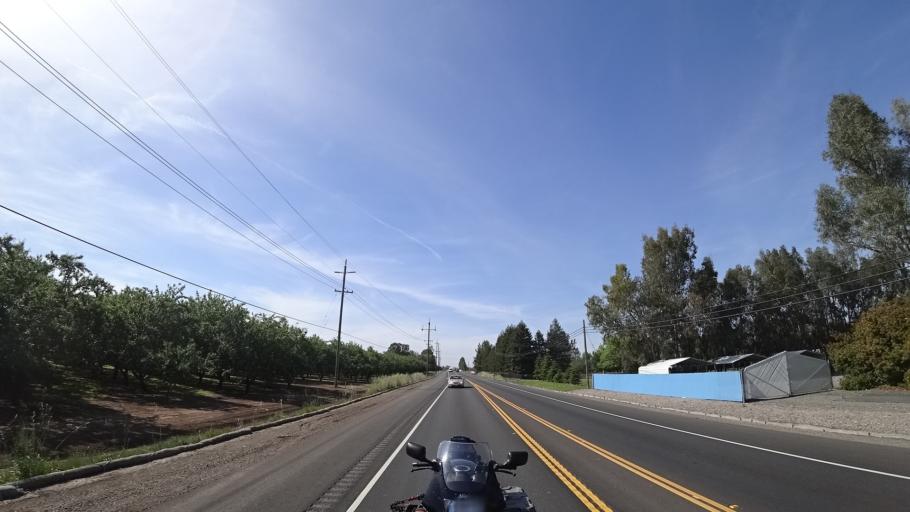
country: US
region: California
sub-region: Glenn County
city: Hamilton City
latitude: 39.8170
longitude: -121.9206
